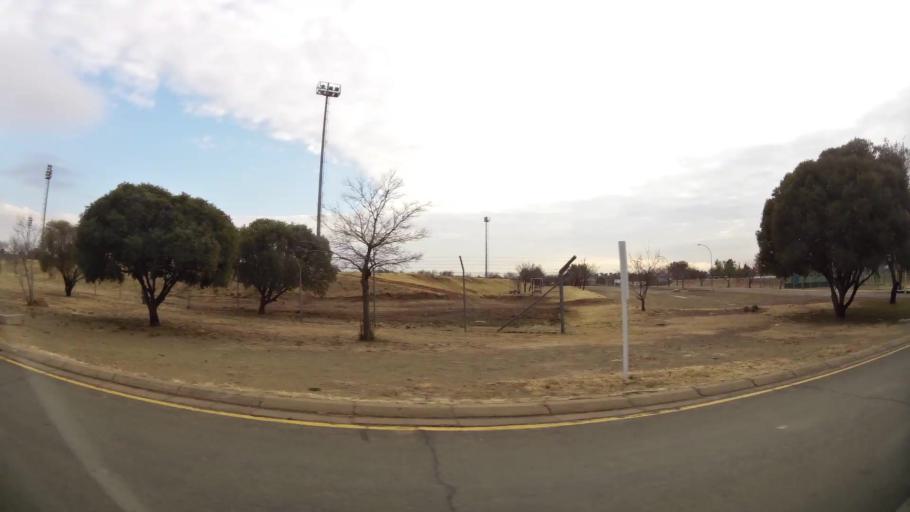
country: ZA
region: Orange Free State
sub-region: Mangaung Metropolitan Municipality
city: Bloemfontein
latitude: -29.1097
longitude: 26.1750
